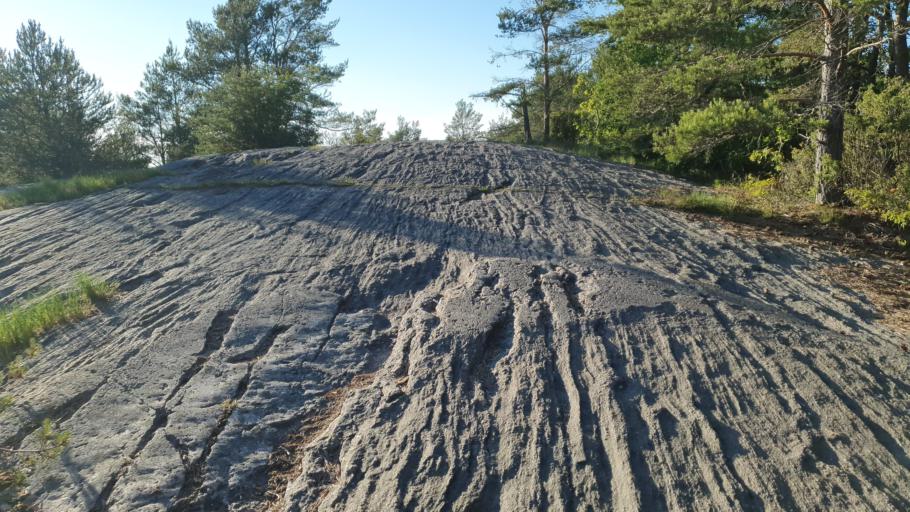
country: SE
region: Vaestra Goetaland
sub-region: Molndal
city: Kallered
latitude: 57.6396
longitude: 12.0507
